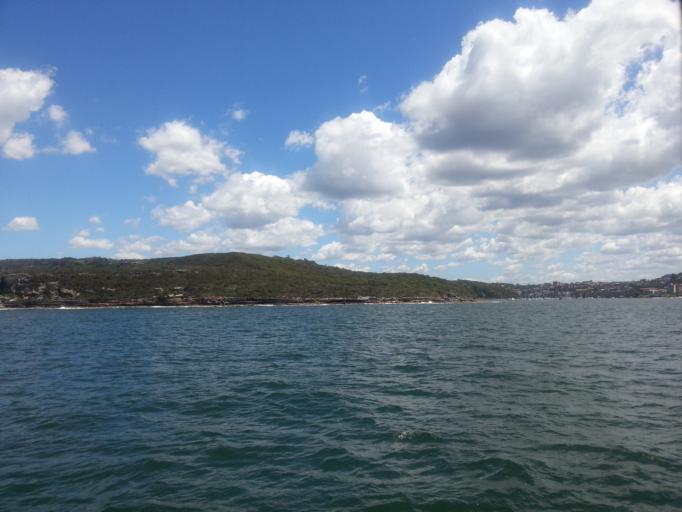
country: AU
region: New South Wales
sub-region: Manly Vale
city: Manly
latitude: -33.8125
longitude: 151.2798
